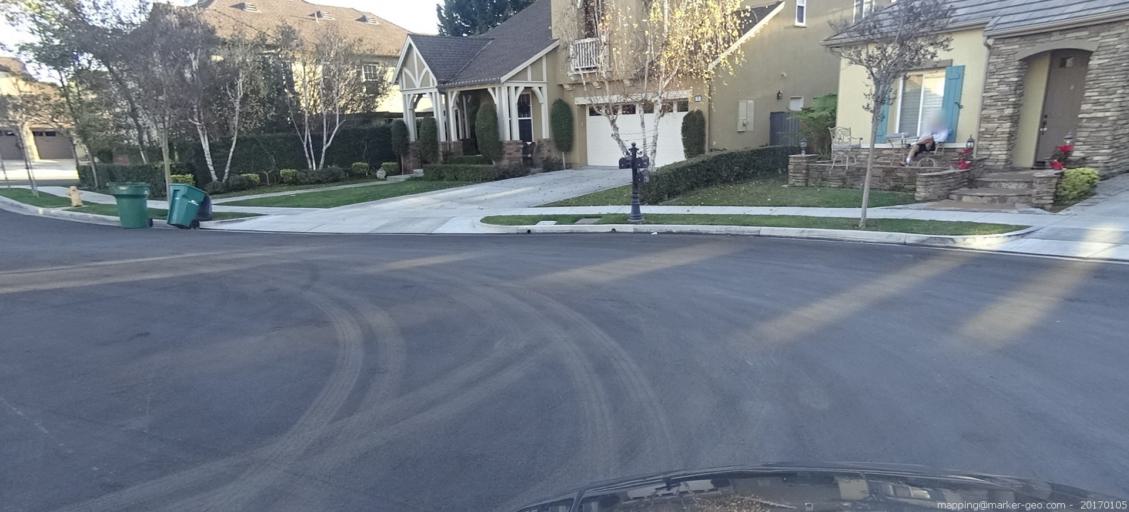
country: US
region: California
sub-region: Orange County
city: Ladera Ranch
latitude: 33.5582
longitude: -117.6347
